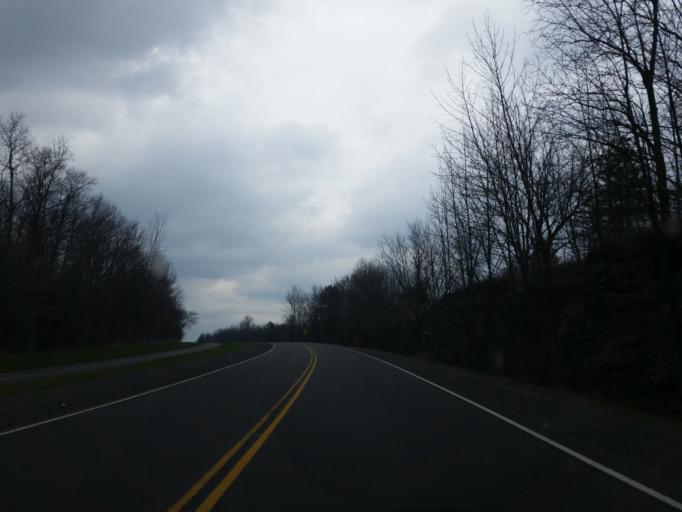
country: CA
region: Ontario
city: Brockville
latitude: 44.4909
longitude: -75.8170
